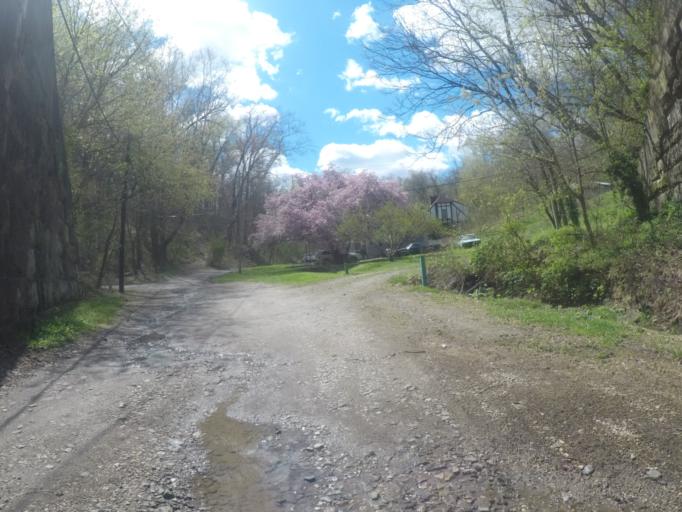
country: US
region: West Virginia
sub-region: Wayne County
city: Kenova
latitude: 38.3984
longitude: -82.5858
